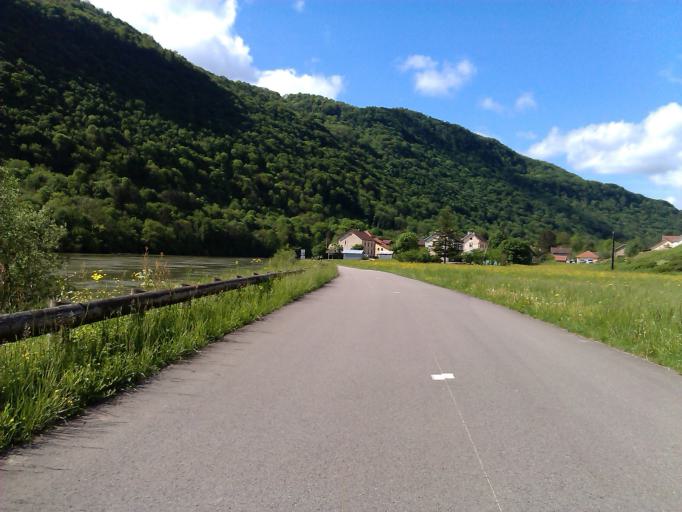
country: FR
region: Franche-Comte
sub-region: Departement du Doubs
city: Roulans
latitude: 47.3142
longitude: 6.2614
